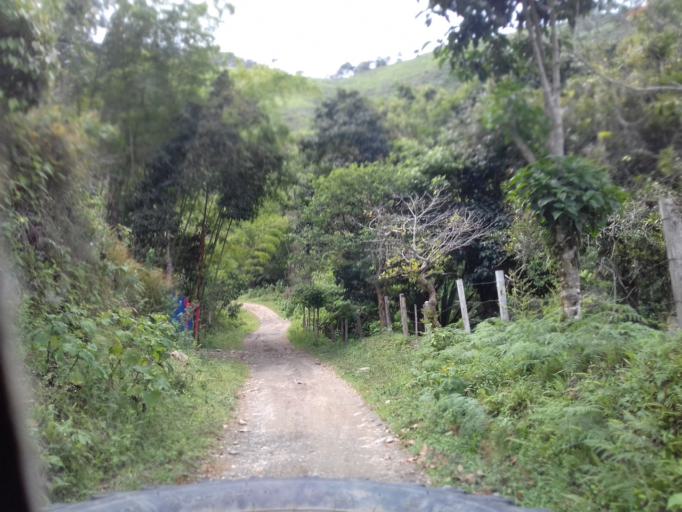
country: CO
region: Tolima
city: Libano
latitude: 4.9287
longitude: -75.0881
